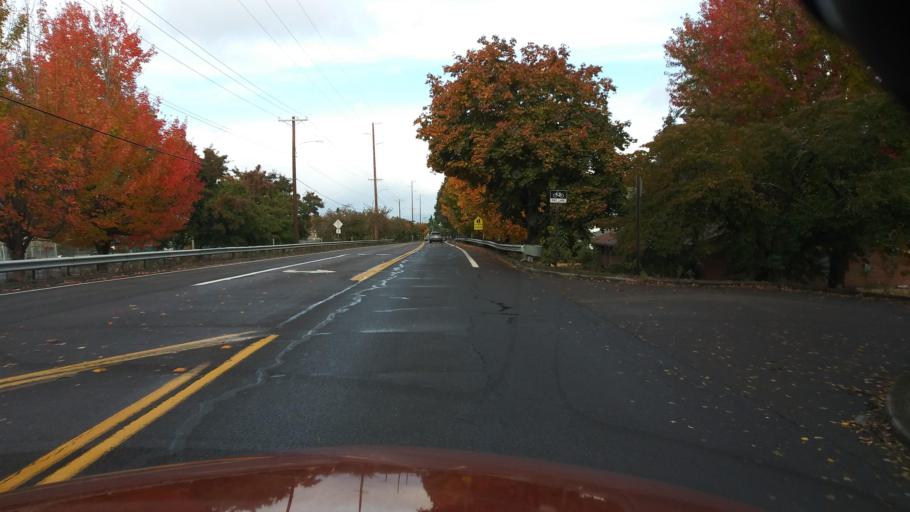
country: US
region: Oregon
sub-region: Washington County
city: Forest Grove
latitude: 45.5207
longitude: -123.1215
